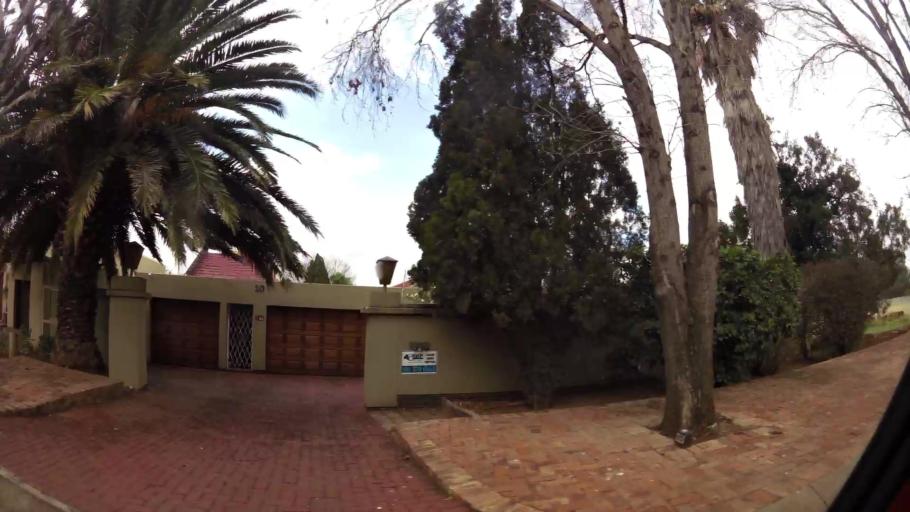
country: ZA
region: Gauteng
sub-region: Sedibeng District Municipality
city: Vanderbijlpark
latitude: -26.7394
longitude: 27.8512
